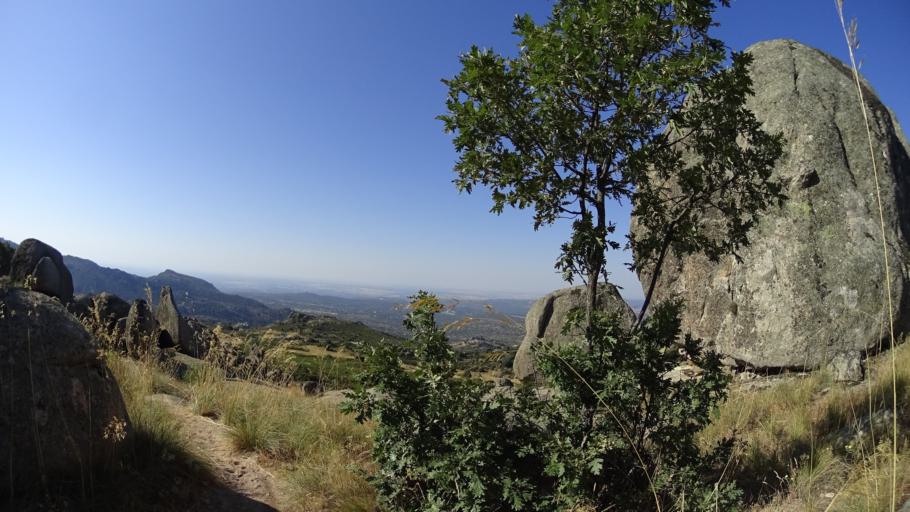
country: ES
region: Madrid
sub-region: Provincia de Madrid
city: Moralzarzal
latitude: 40.6508
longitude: -3.9466
